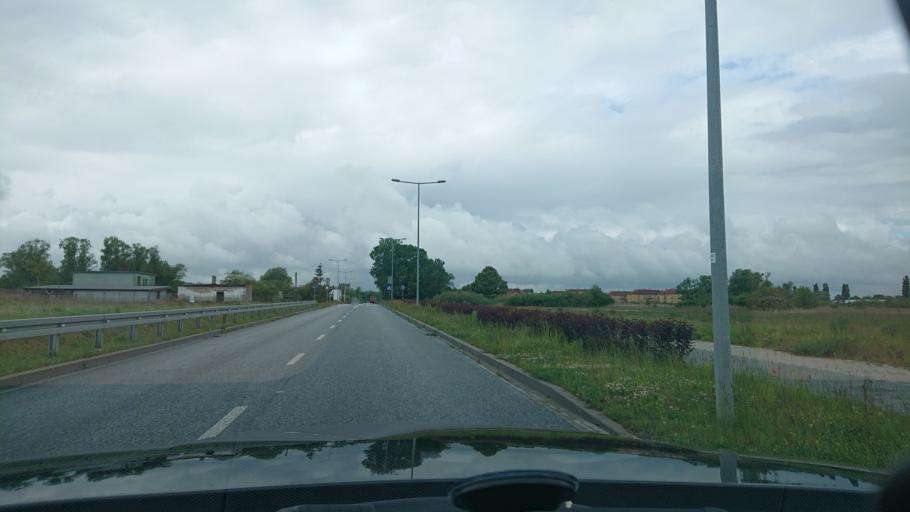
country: PL
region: Greater Poland Voivodeship
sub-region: Powiat gnieznienski
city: Gniezno
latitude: 52.5236
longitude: 17.6231
